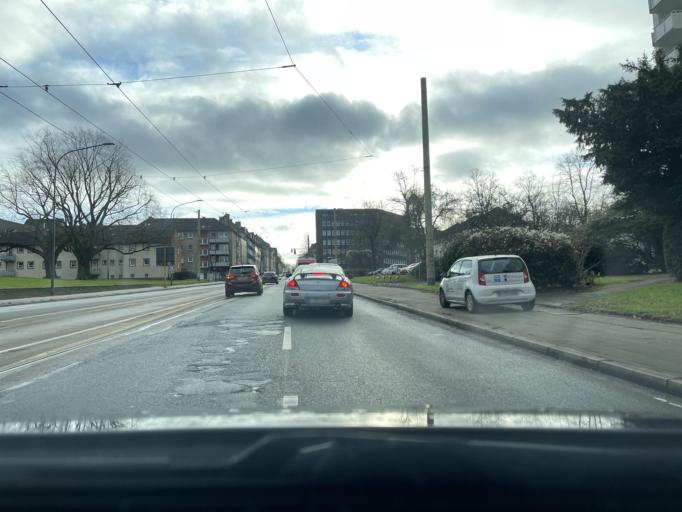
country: DE
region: North Rhine-Westphalia
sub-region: Regierungsbezirk Dusseldorf
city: Essen
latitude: 51.4437
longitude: 6.9868
